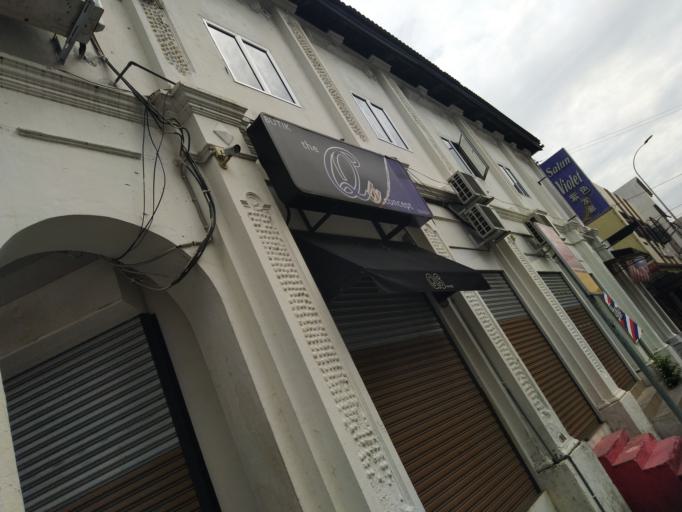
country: MY
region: Perak
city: Ipoh
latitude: 4.5978
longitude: 101.0860
